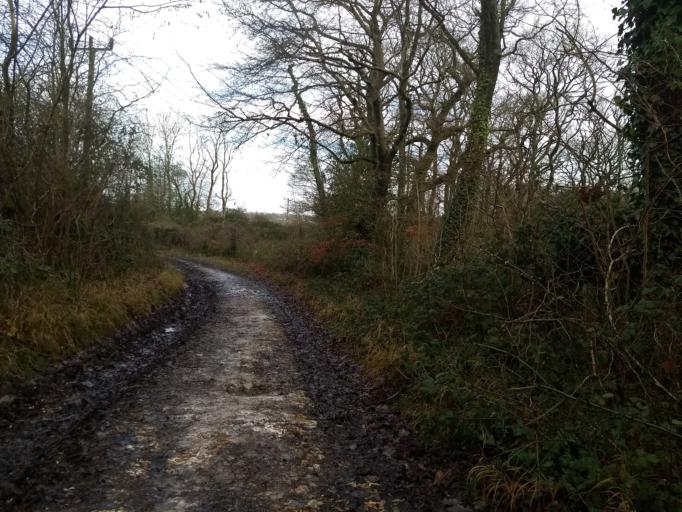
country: GB
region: England
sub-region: Isle of Wight
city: Newchurch
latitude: 50.7151
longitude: -1.2315
